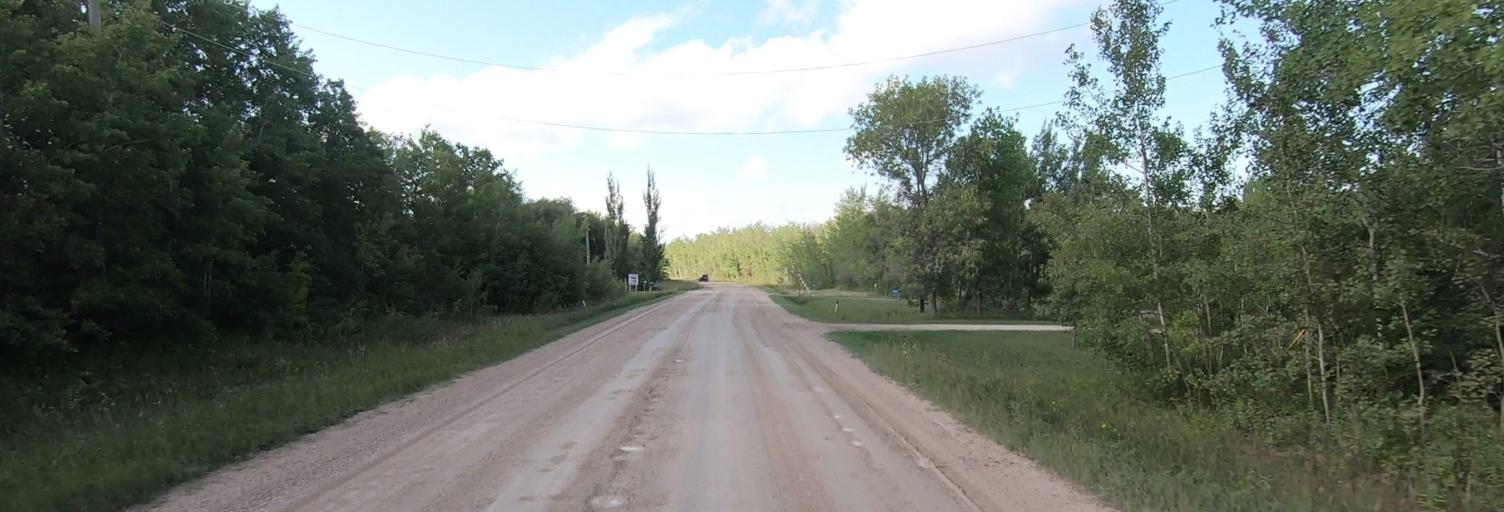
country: CA
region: Manitoba
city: Selkirk
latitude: 50.2299
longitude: -96.8400
